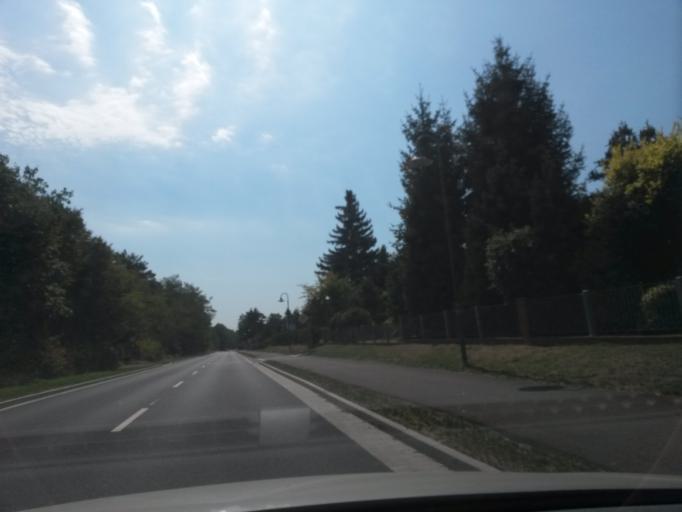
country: DE
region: Saxony-Anhalt
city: Jerichow
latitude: 52.4300
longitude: 11.9969
